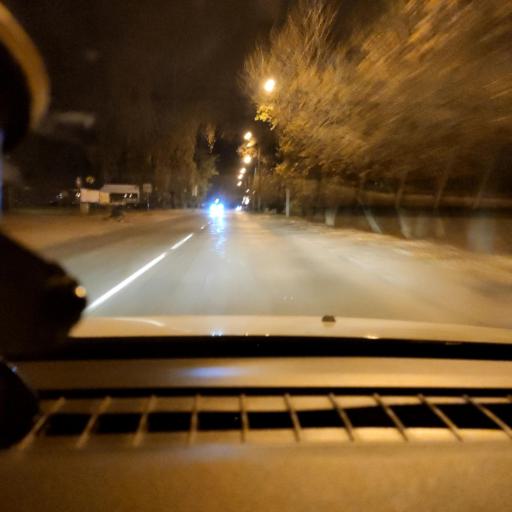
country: RU
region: Samara
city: Rozhdestveno
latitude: 53.1432
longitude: 50.0403
